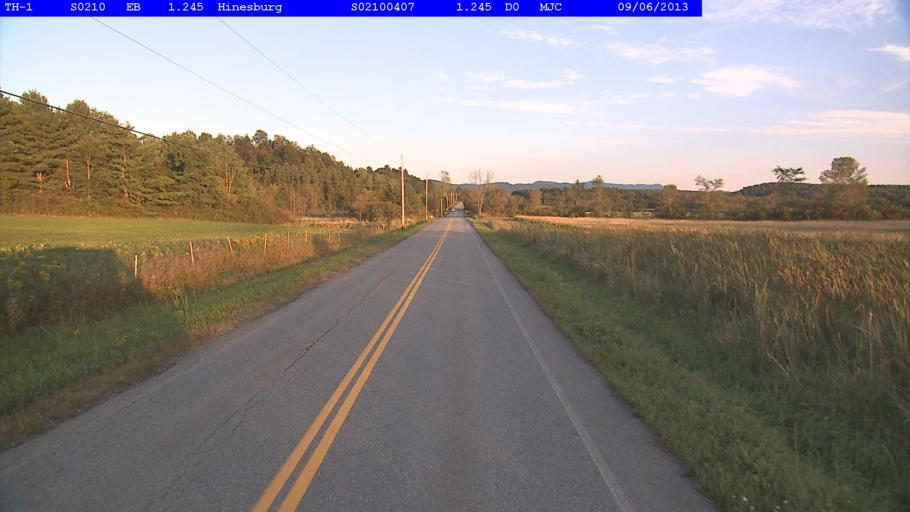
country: US
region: Vermont
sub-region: Chittenden County
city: Hinesburg
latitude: 44.3484
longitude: -73.1471
